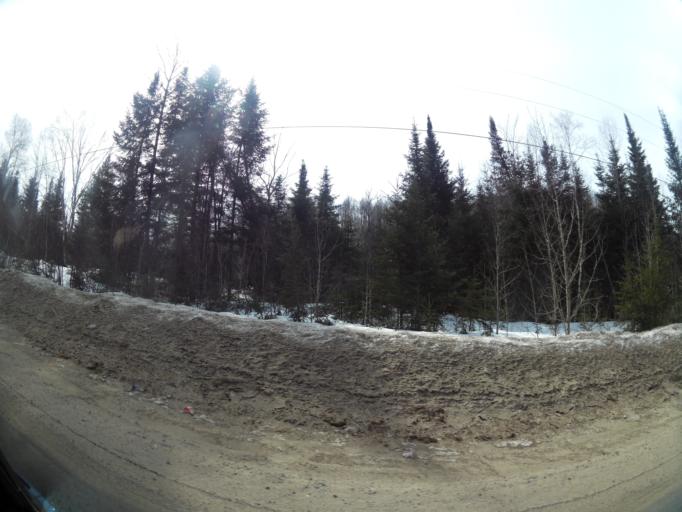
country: CA
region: Quebec
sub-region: Outaouais
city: Val-des-Monts
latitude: 45.9702
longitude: -75.5393
